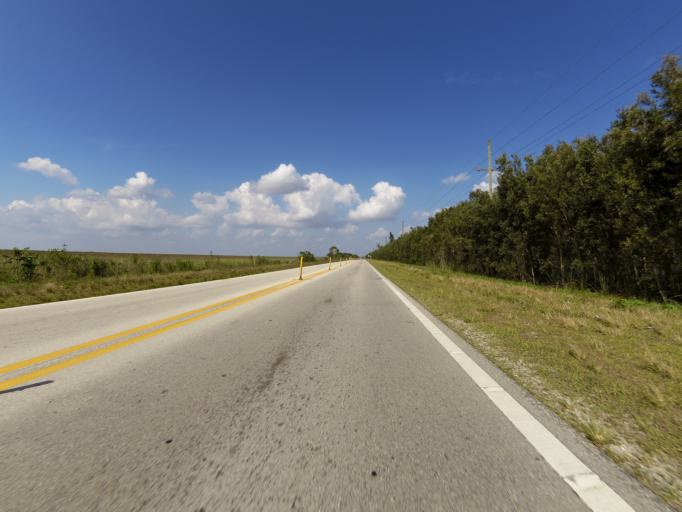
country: US
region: Florida
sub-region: Miami-Dade County
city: Palm Springs North
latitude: 25.9168
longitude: -80.4619
